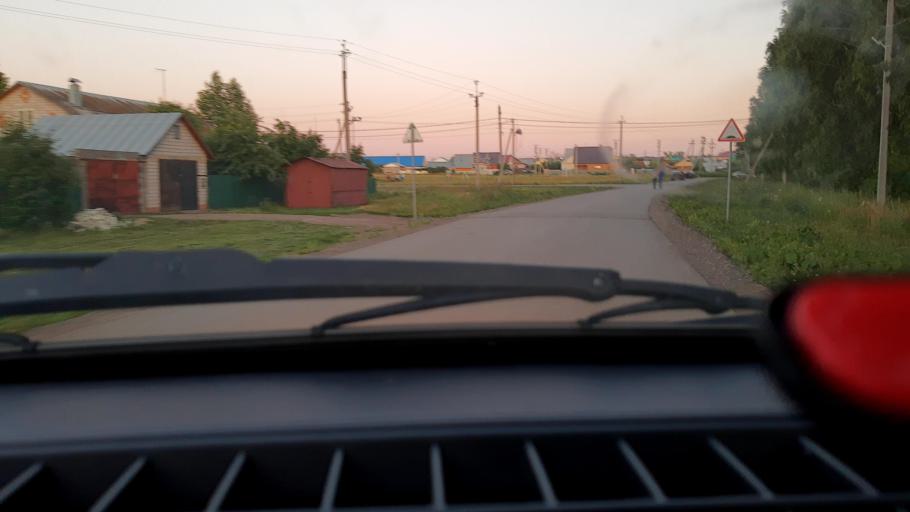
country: RU
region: Bashkortostan
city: Avdon
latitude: 54.4984
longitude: 55.8996
